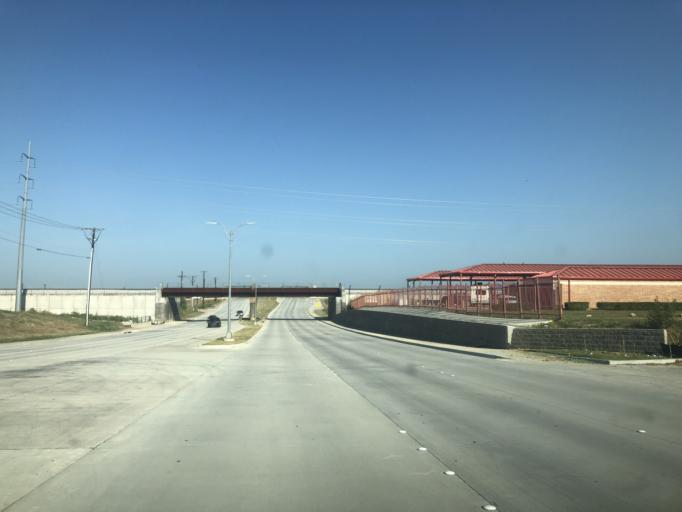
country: US
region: Texas
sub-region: Tarrant County
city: Benbrook
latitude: 32.6446
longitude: -97.4122
